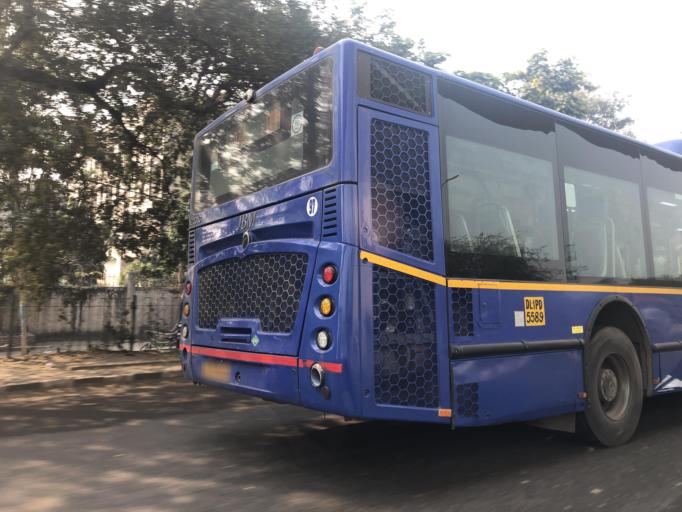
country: IN
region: NCT
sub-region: North West Delhi
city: Pitampura
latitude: 28.6746
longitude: 77.1327
